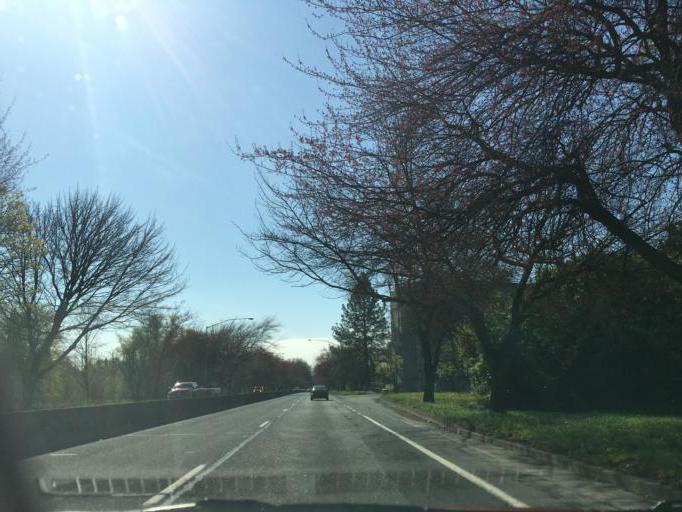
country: US
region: Oregon
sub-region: Clackamas County
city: Milwaukie
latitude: 45.4787
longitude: -122.6415
